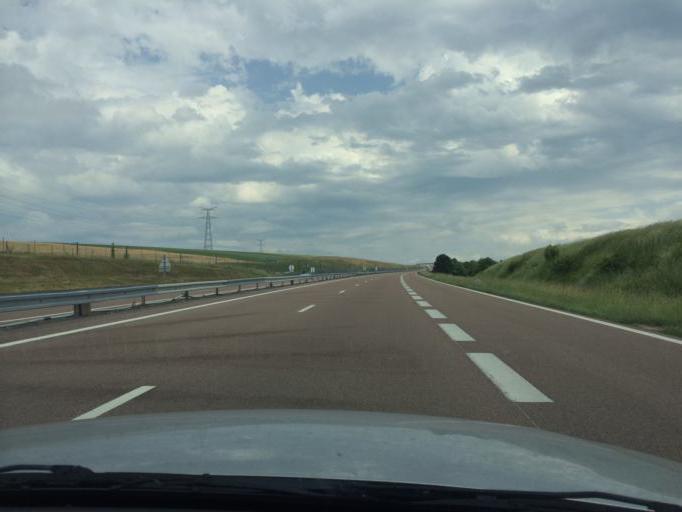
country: FR
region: Champagne-Ardenne
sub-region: Departement de la Marne
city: Jonchery-sur-Vesle
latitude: 49.2273
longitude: 3.8252
